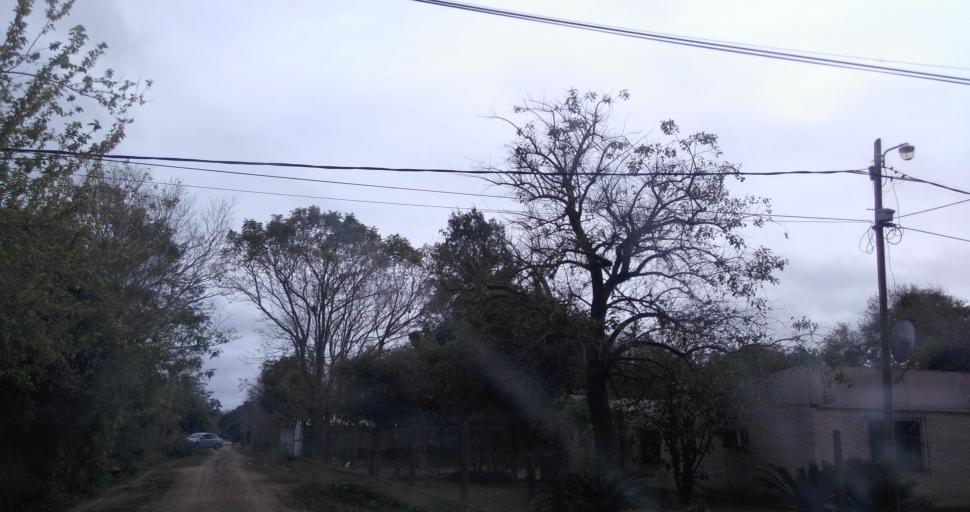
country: AR
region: Chaco
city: Colonia Benitez
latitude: -27.3289
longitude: -58.9525
